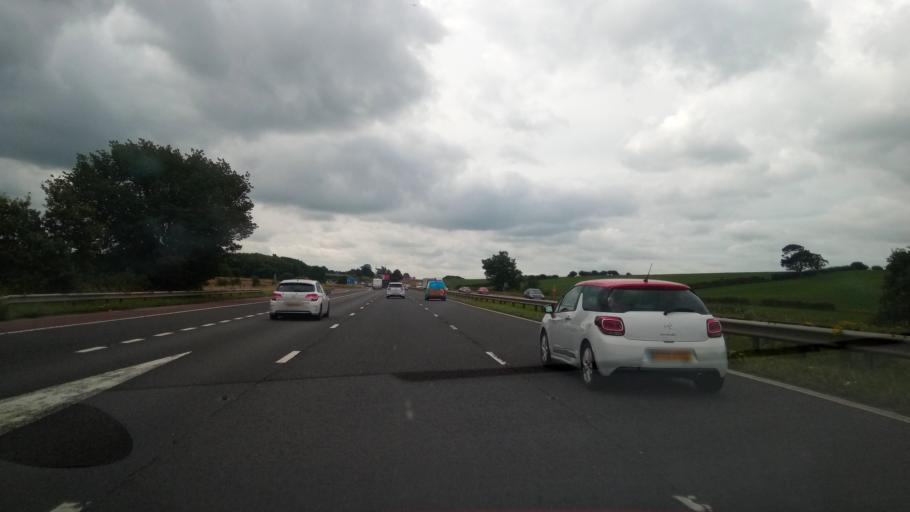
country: GB
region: England
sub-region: Lancashire
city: Galgate
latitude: 53.9885
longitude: -2.7812
